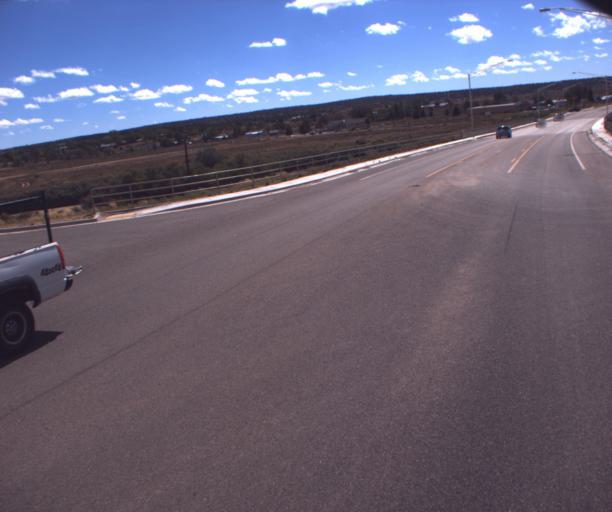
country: US
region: Arizona
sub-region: Apache County
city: Houck
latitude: 35.2132
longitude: -109.3318
